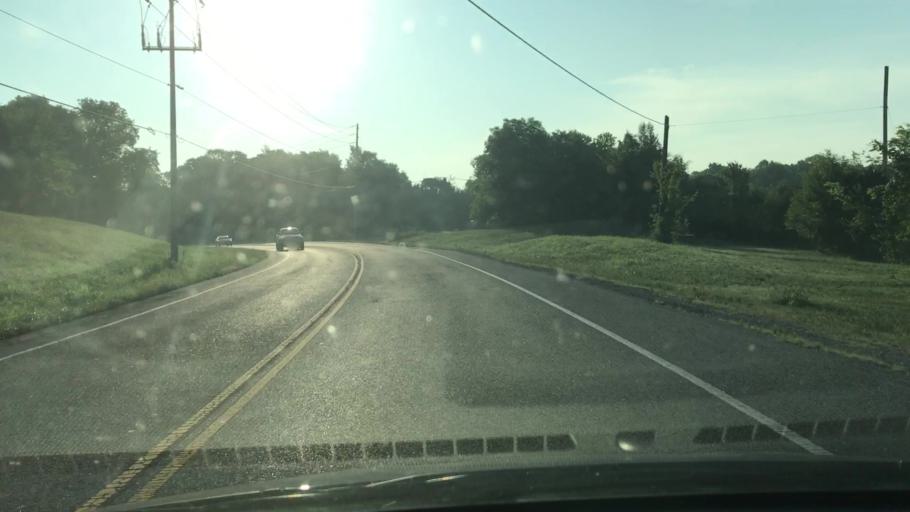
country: US
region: Tennessee
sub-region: Rutherford County
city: La Vergne
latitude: 35.9895
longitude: -86.6278
